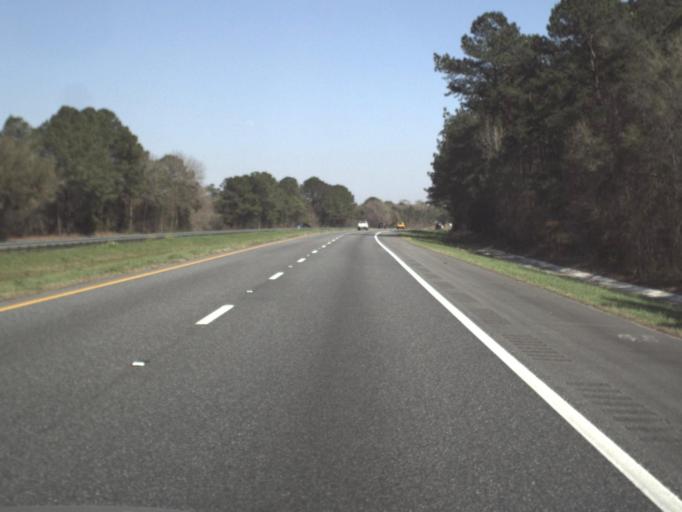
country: US
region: Florida
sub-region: Jackson County
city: Marianna
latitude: 30.7576
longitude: -85.3165
